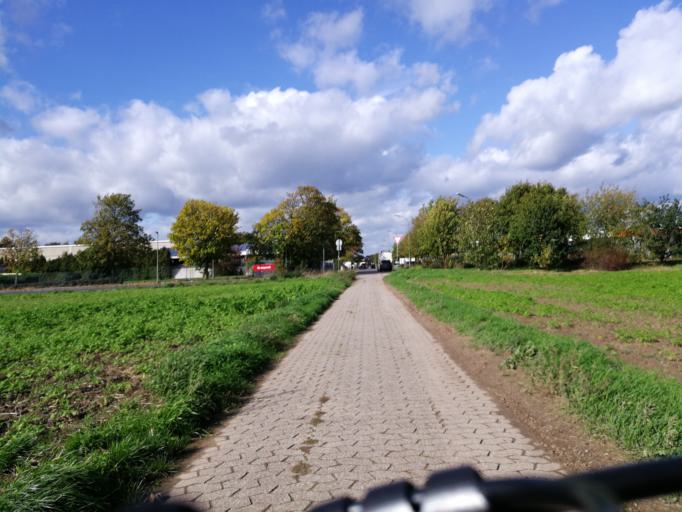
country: DE
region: North Rhine-Westphalia
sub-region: Regierungsbezirk Dusseldorf
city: Dusseldorf
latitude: 51.1550
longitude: 6.7458
